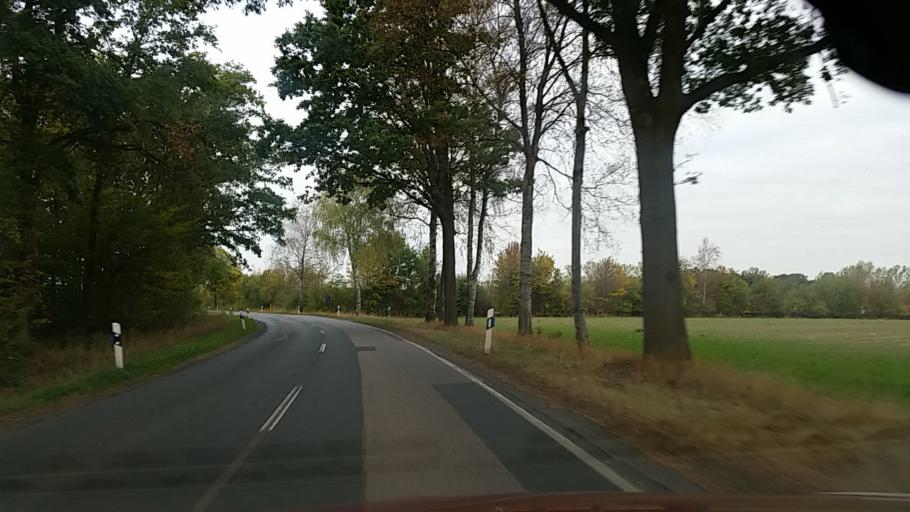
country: DE
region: Lower Saxony
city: Hohne
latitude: 52.5921
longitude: 10.3947
